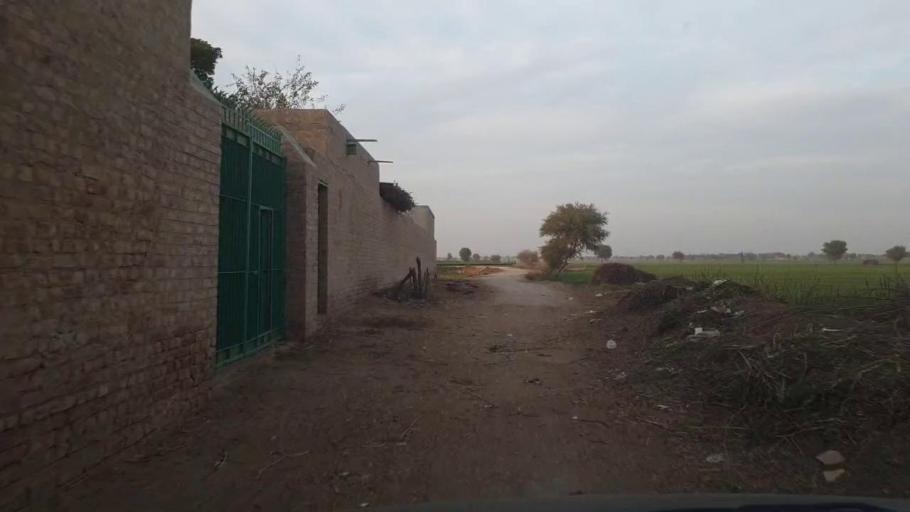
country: PK
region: Sindh
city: Shahpur Chakar
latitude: 26.0763
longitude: 68.5324
